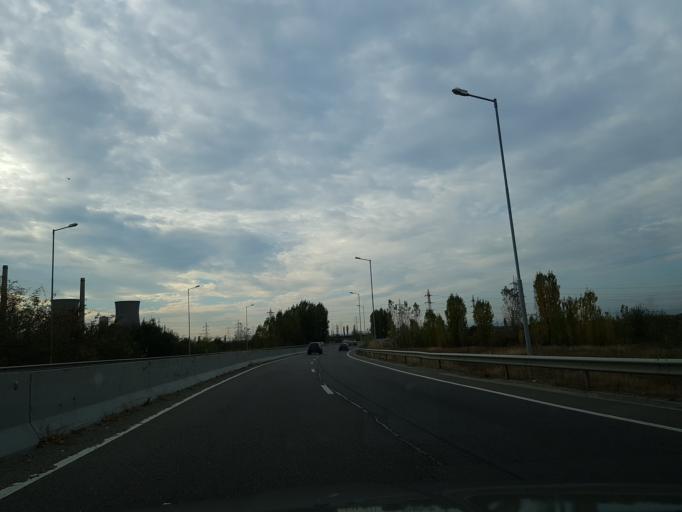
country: RO
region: Prahova
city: Brazii de Sus
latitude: 44.8848
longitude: 26.0168
